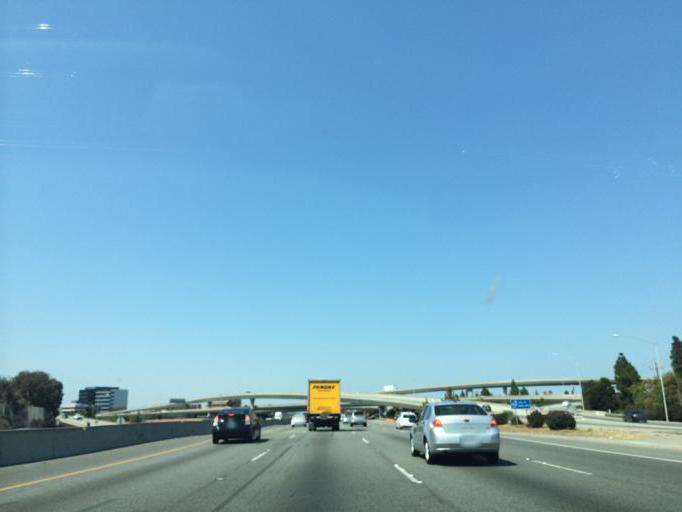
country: US
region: California
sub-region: San Mateo County
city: Foster City
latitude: 37.5504
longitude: -122.2932
